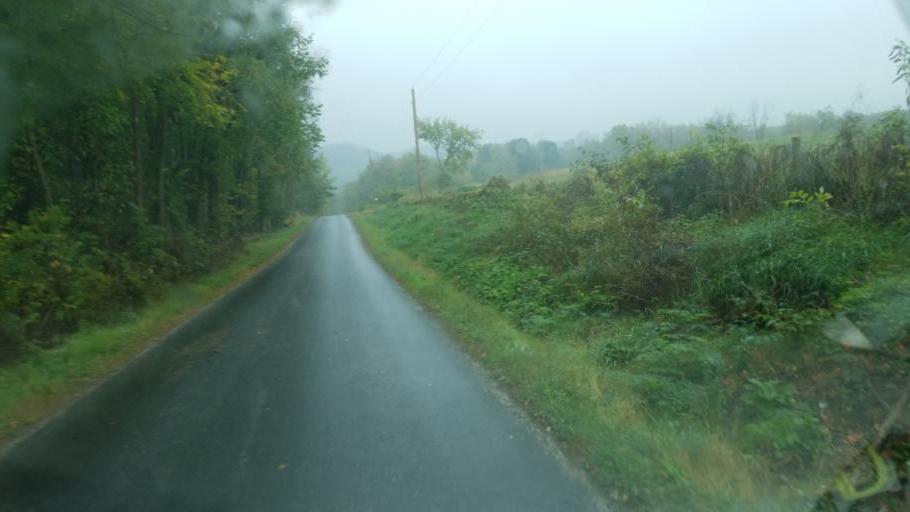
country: US
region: Ohio
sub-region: Tuscarawas County
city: Sugarcreek
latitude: 40.5795
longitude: -81.7410
